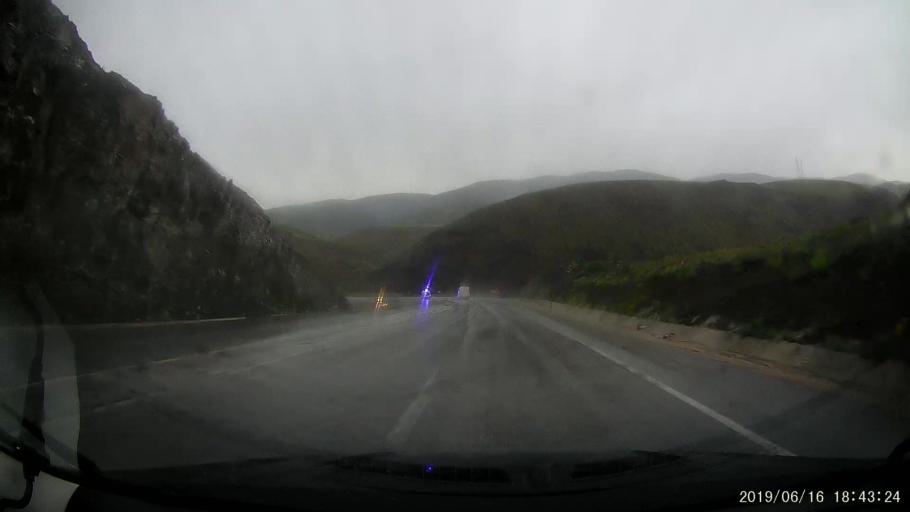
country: TR
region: Erzincan
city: Doganbeyli
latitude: 39.8692
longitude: 39.0917
